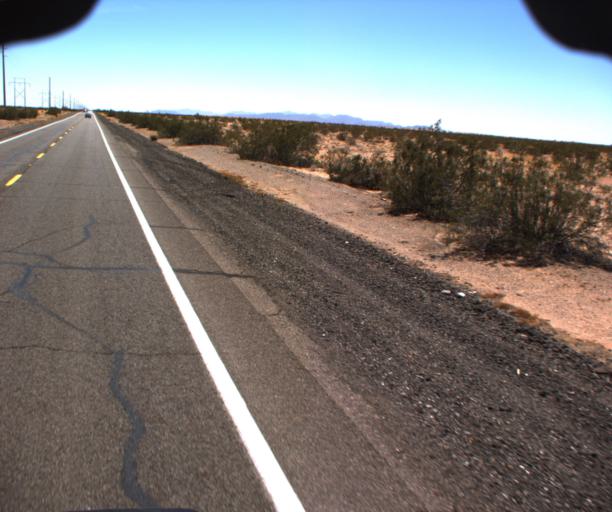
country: US
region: Arizona
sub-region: La Paz County
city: Parker
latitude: 33.9169
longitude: -114.2169
